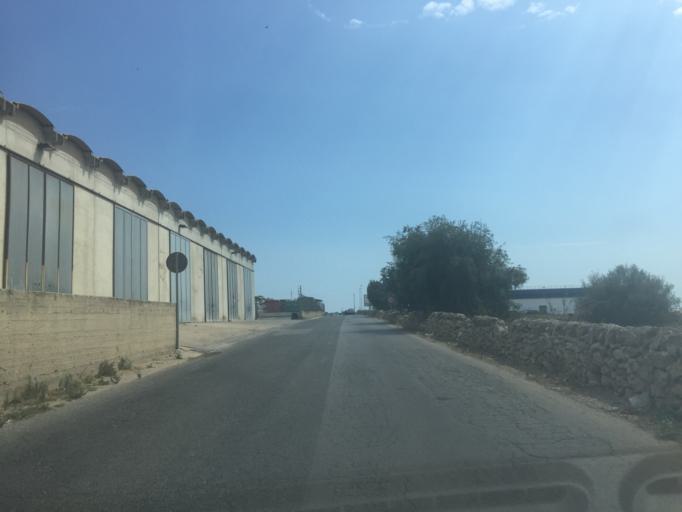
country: IT
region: Sicily
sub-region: Ragusa
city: Santa Croce Camerina
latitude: 36.8274
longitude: 14.5192
